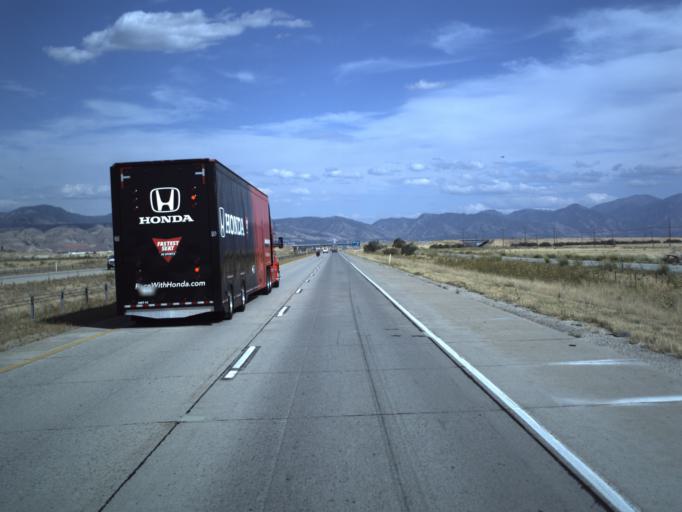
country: US
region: Utah
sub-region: Salt Lake County
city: Magna
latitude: 40.7708
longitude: -112.0763
